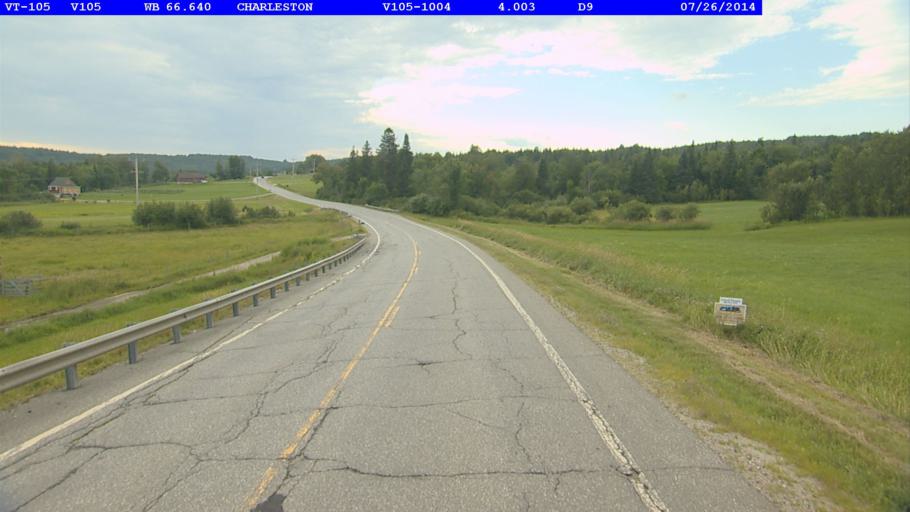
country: US
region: Vermont
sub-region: Orleans County
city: Newport
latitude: 44.8625
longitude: -72.0377
